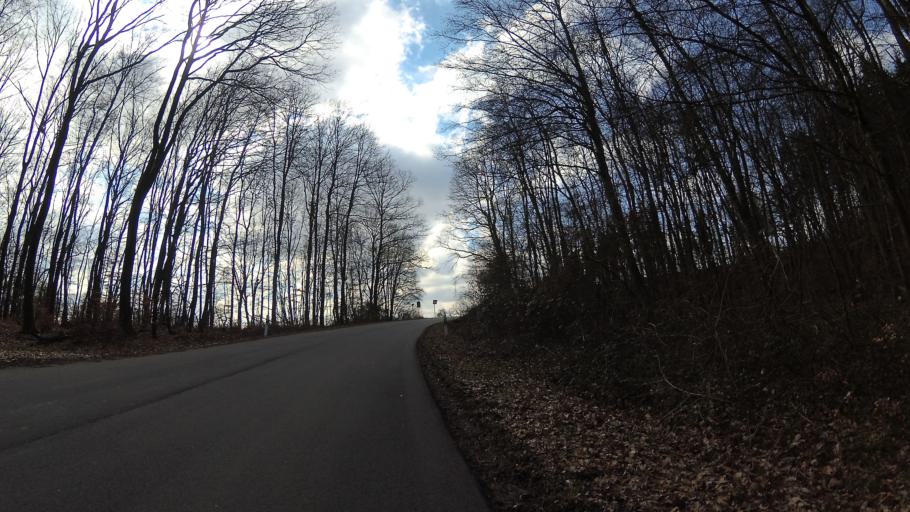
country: DE
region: Saarland
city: Rehlingen-Siersburg
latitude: 49.3873
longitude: 6.6607
